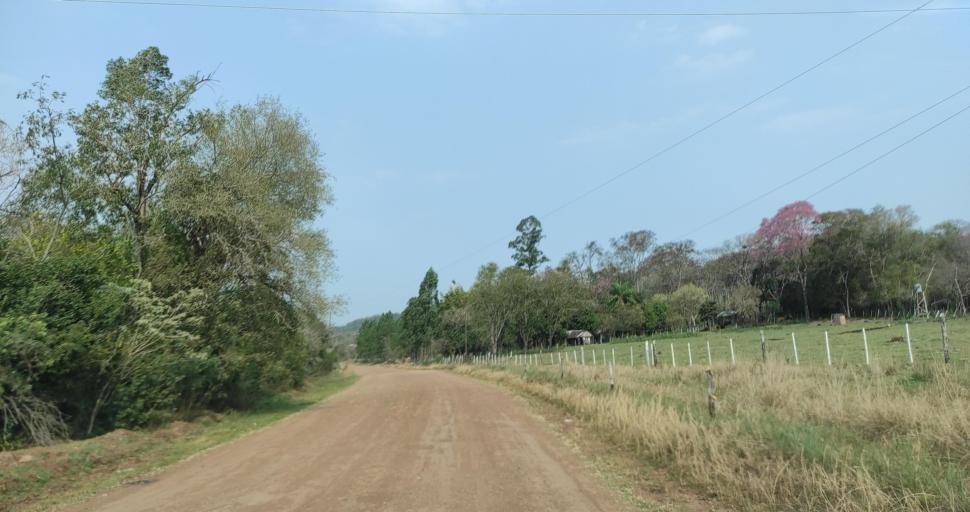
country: AR
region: Misiones
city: Cerro Cora
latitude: -27.5163
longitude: -55.6030
